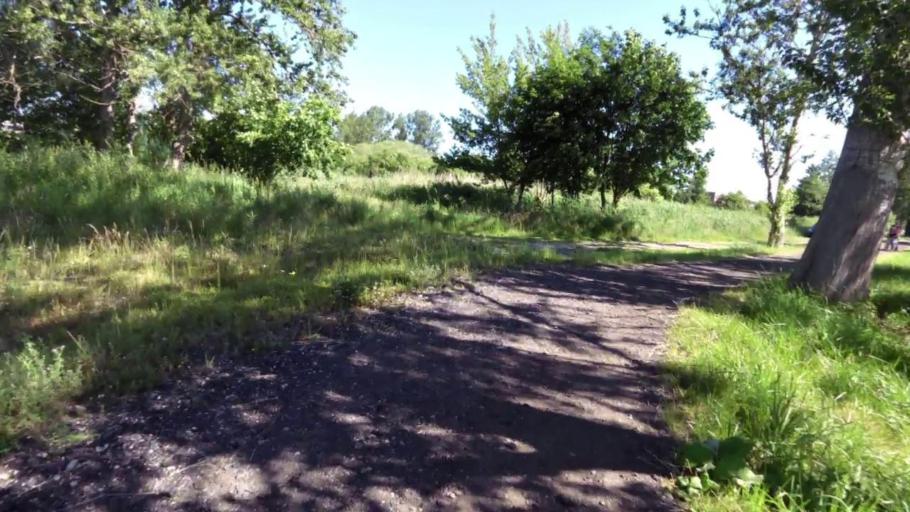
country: PL
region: West Pomeranian Voivodeship
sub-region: Powiat koszalinski
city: Mielno
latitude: 54.2742
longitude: 16.1166
